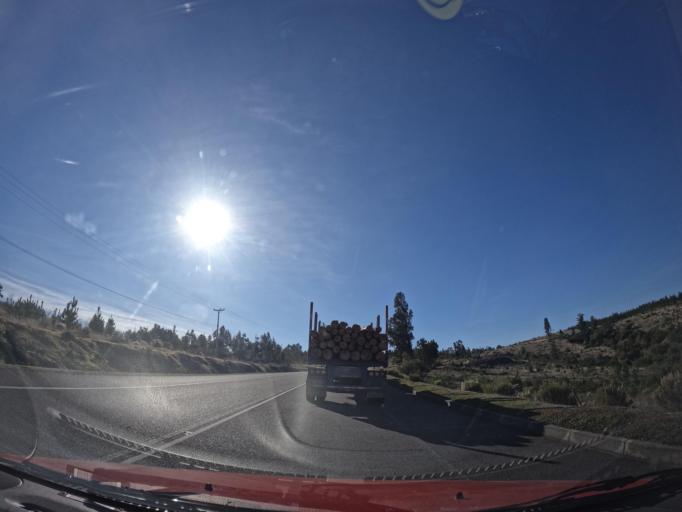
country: CL
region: Maule
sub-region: Provincia de Cauquenes
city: Cauquenes
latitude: -35.9357
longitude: -72.1956
